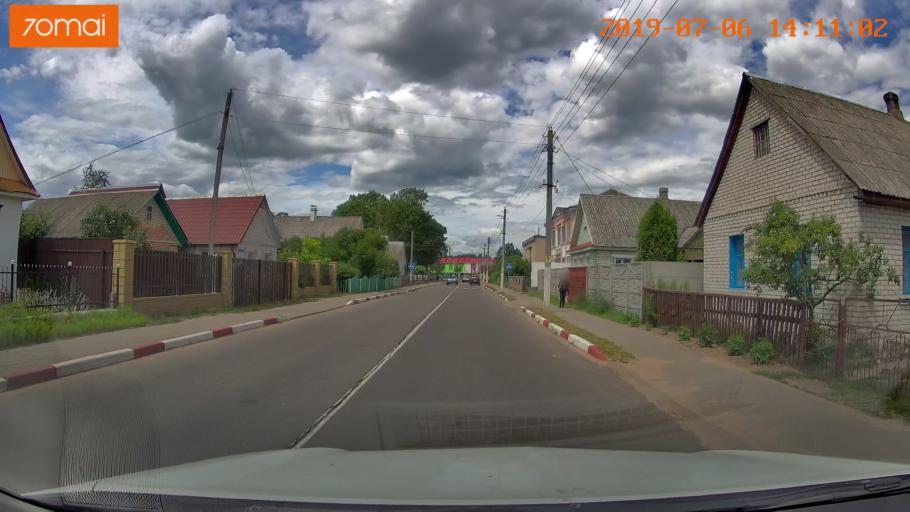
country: BY
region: Minsk
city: Ivyanyets
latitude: 53.8876
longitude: 26.7423
